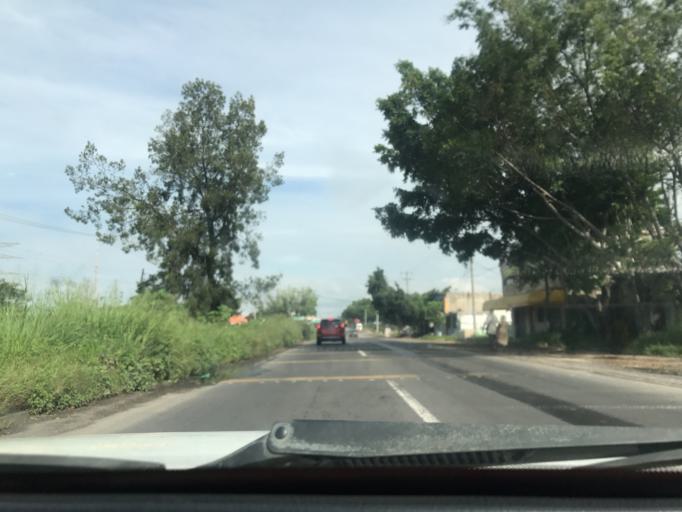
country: MX
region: Morelos
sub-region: Cuautla
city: Tierra Larga (Campo Nuevo)
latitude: 18.8444
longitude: -98.9291
